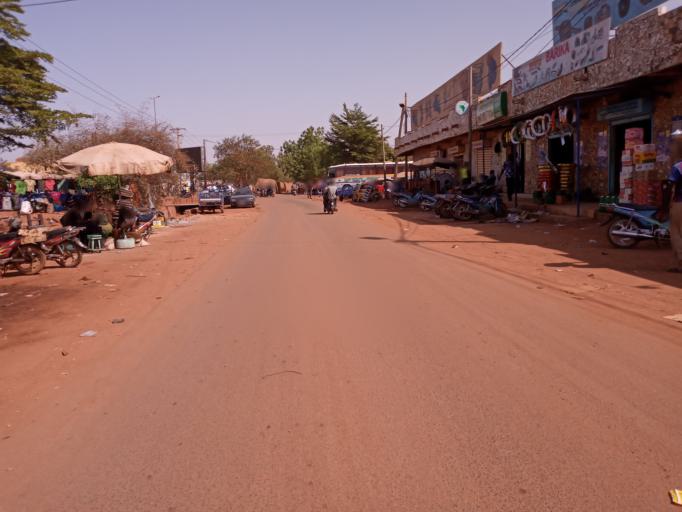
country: ML
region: Bamako
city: Bamako
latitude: 12.5972
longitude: -7.9606
